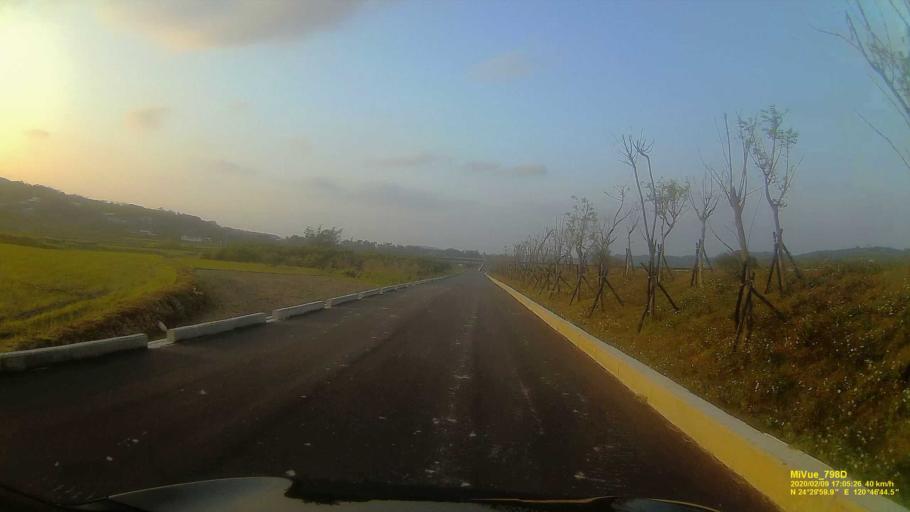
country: TW
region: Taiwan
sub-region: Miaoli
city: Miaoli
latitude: 24.5002
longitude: 120.7789
